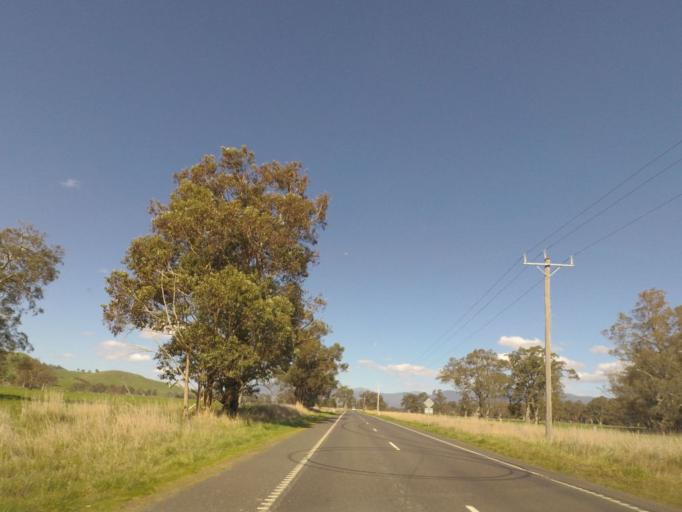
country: AU
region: Victoria
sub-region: Murrindindi
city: Alexandra
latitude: -37.2230
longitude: 145.7390
